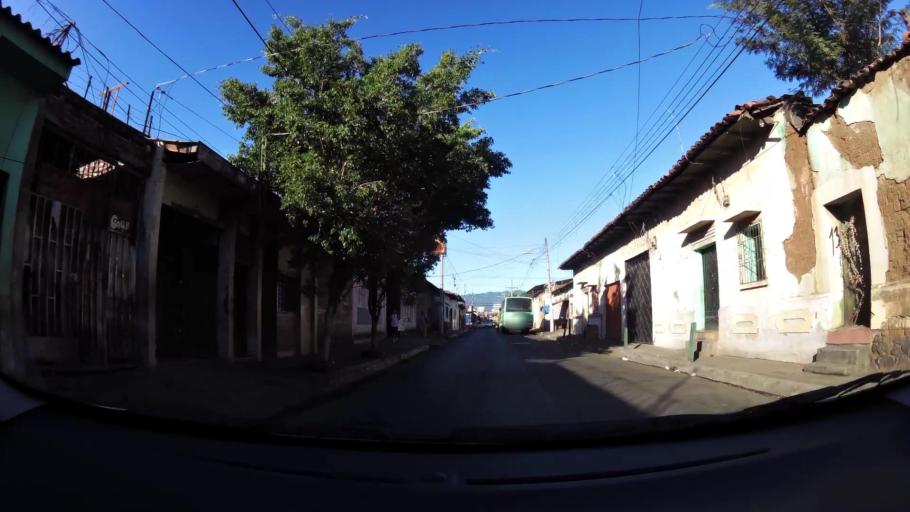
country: SV
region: San Miguel
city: San Miguel
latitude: 13.4855
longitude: -88.1716
